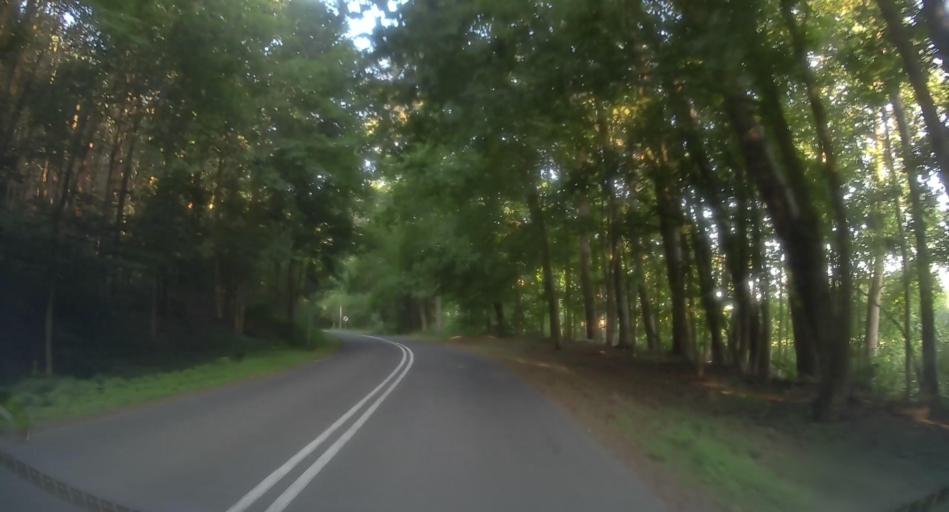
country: PL
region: Lodz Voivodeship
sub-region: Powiat skierniewicki
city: Kowiesy
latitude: 51.8922
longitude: 20.3912
